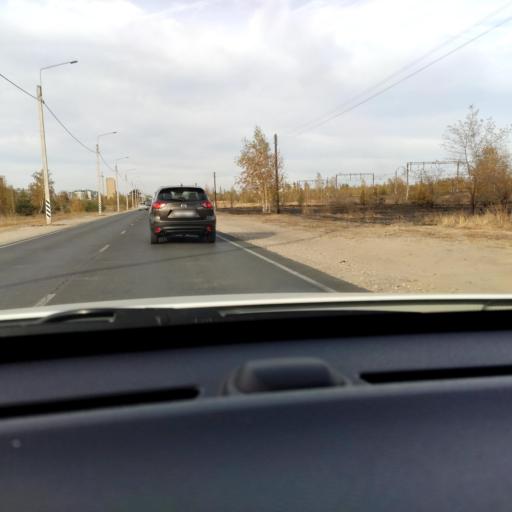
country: RU
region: Voronezj
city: Maslovka
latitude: 51.5799
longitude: 39.2473
